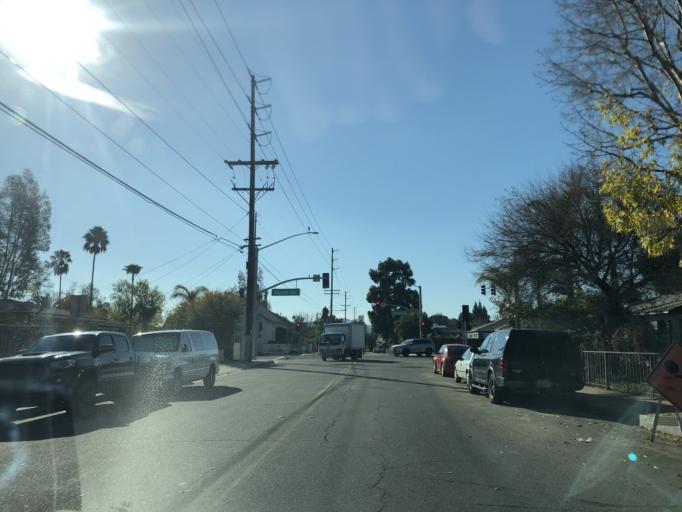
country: US
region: California
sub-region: San Diego County
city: Escondido
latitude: 33.1326
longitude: -117.0902
